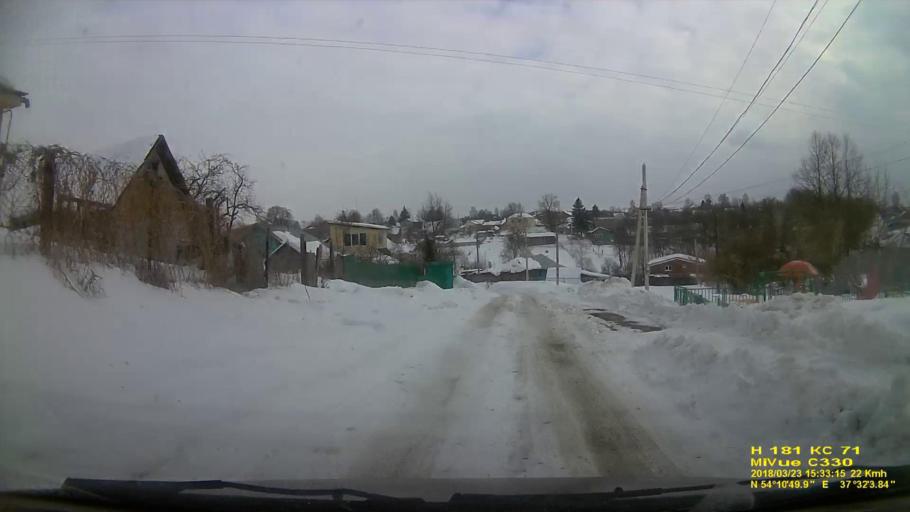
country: RU
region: Tula
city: Kosaya Gora
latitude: 54.1804
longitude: 37.5344
